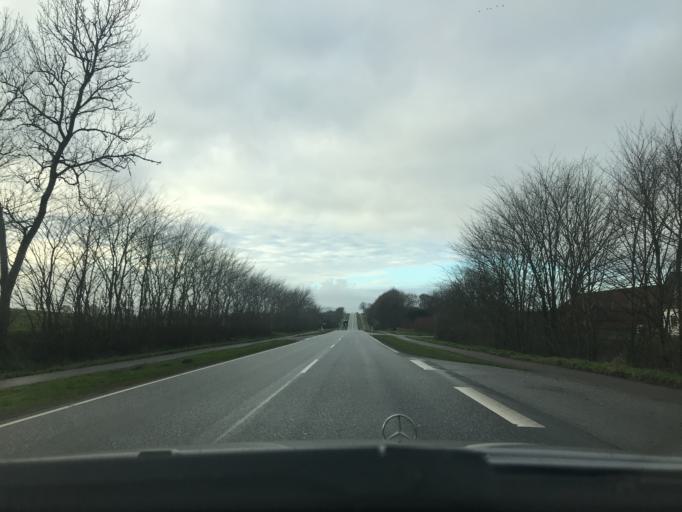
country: DK
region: South Denmark
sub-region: Sonderborg Kommune
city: Dybbol
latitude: 54.9085
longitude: 9.7358
